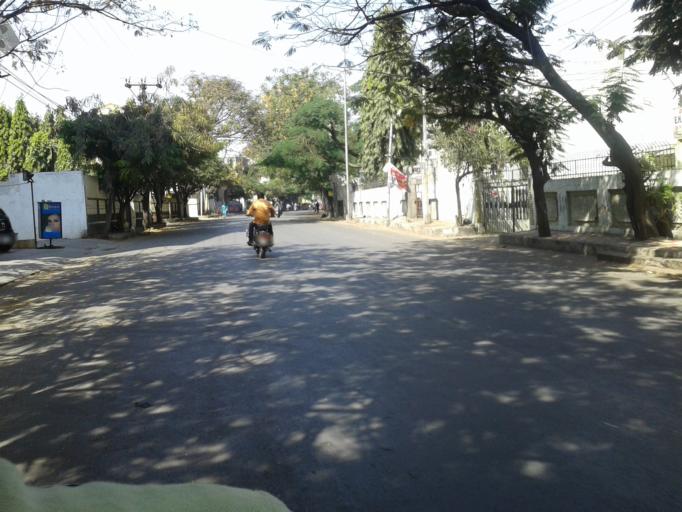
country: IN
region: Telangana
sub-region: Hyderabad
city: Hyderabad
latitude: 17.3912
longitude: 78.4848
